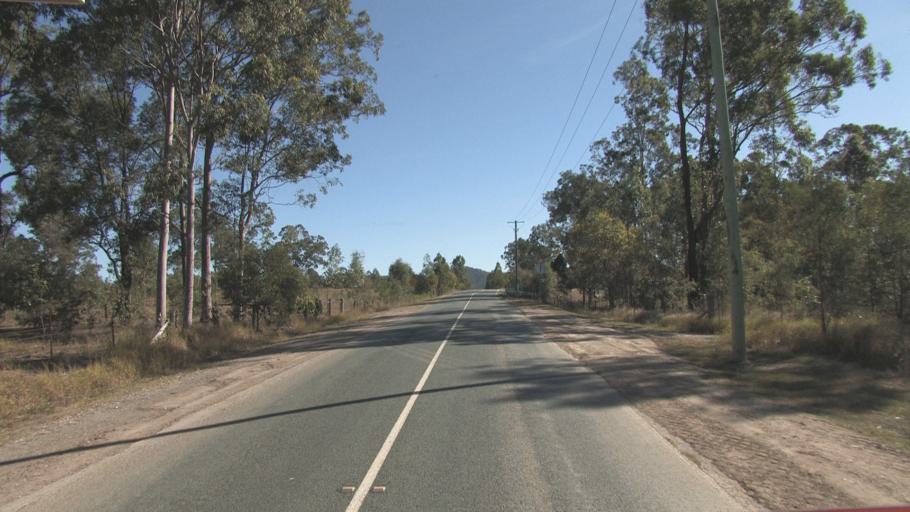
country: AU
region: Queensland
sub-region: Ipswich
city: Springfield Lakes
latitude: -27.7315
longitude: 152.9382
